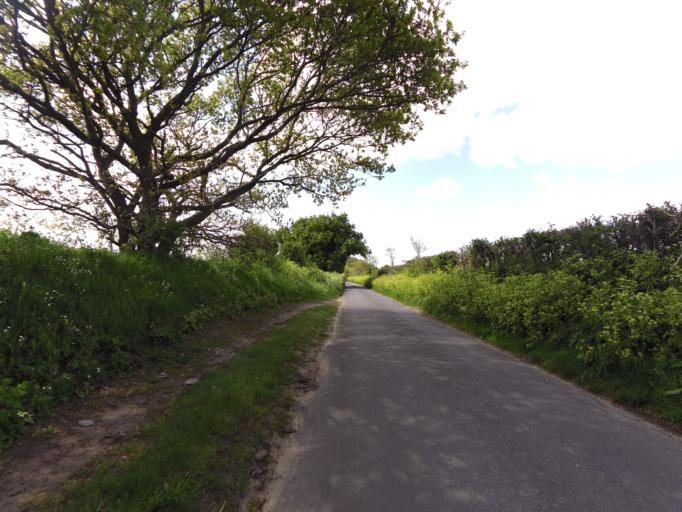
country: GB
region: England
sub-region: Suffolk
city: Kessingland
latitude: 52.4412
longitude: 1.6613
